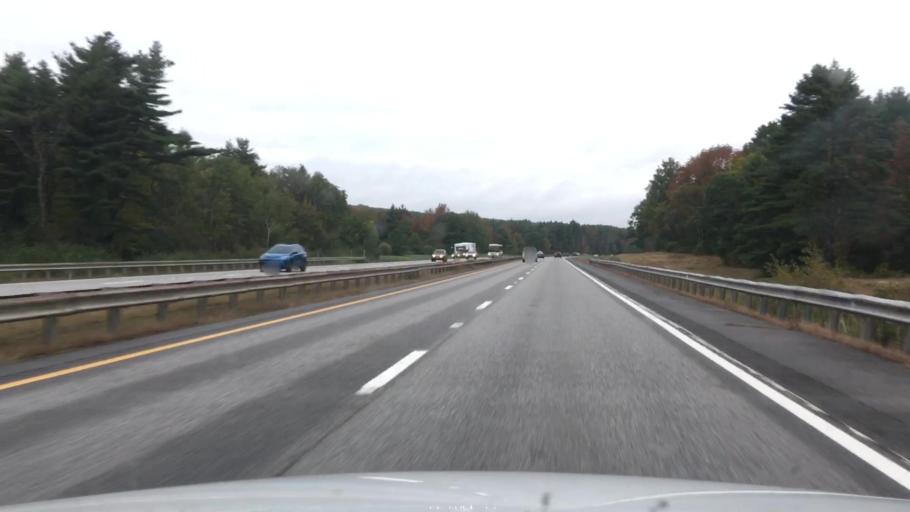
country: US
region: Maine
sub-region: Cumberland County
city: Cumberland Center
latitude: 43.7599
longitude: -70.3082
